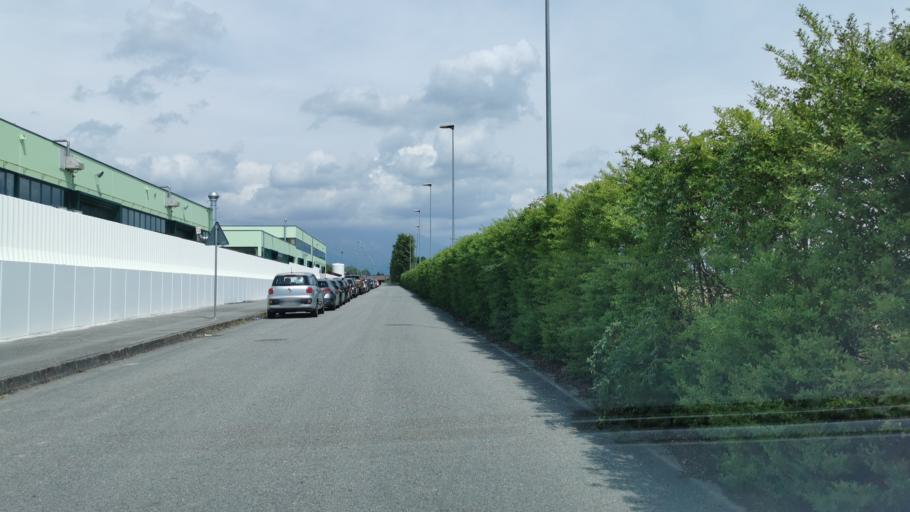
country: IT
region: Piedmont
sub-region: Provincia di Torino
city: Front
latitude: 45.2999
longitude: 7.6704
